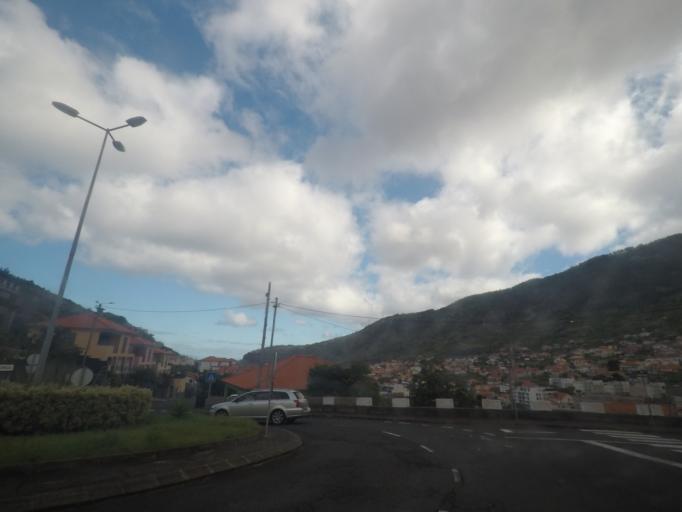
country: PT
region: Madeira
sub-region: Machico
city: Machico
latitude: 32.7295
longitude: -16.7716
